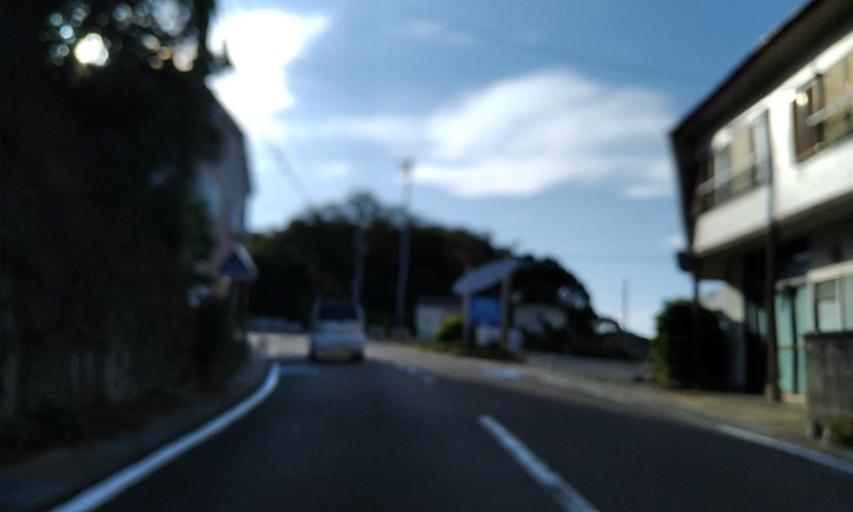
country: JP
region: Wakayama
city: Tanabe
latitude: 33.6936
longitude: 135.3411
